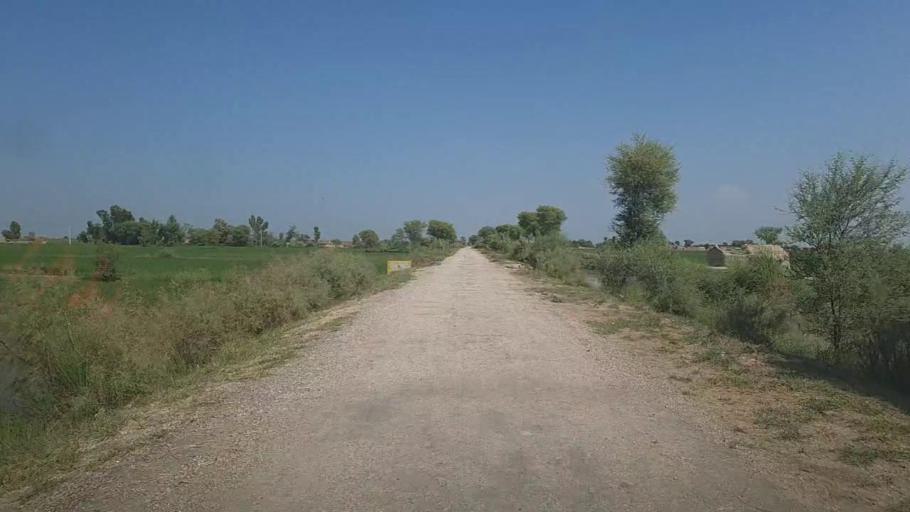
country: PK
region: Sindh
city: Kandhkot
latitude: 28.2975
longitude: 69.1967
